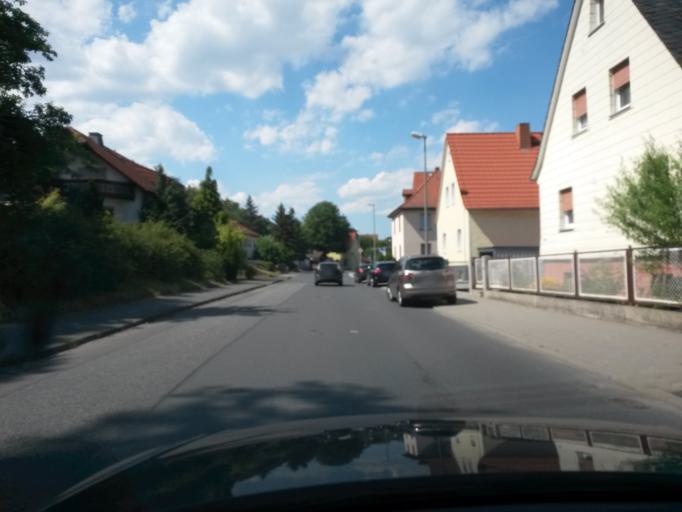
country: DE
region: Hesse
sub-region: Regierungsbezirk Darmstadt
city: Neu-Anspach
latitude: 50.2987
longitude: 8.5165
